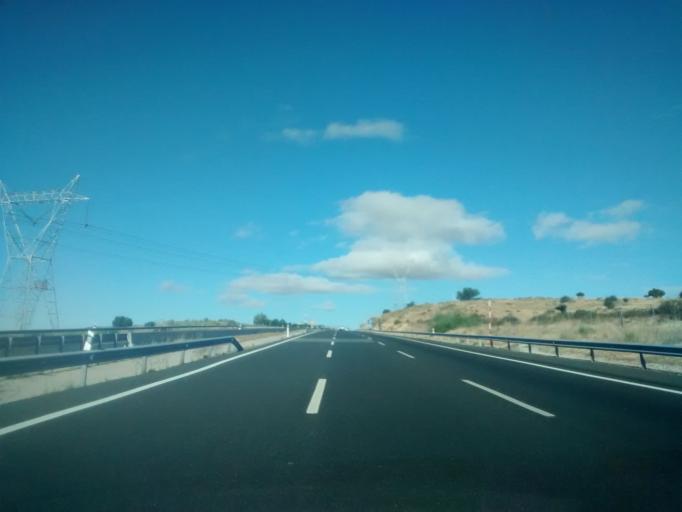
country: ES
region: Castille and Leon
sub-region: Provincia de Segovia
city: Vegas de Matute
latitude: 40.7448
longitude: -4.2842
